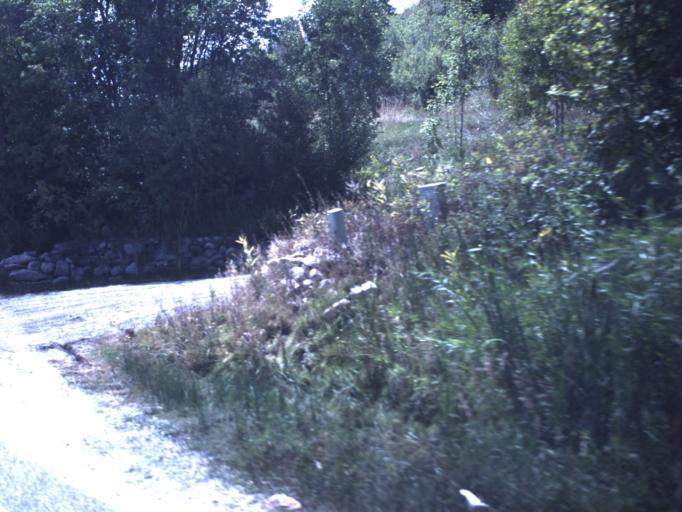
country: US
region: Idaho
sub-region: Bear Lake County
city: Paris
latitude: 41.9768
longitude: -111.4028
